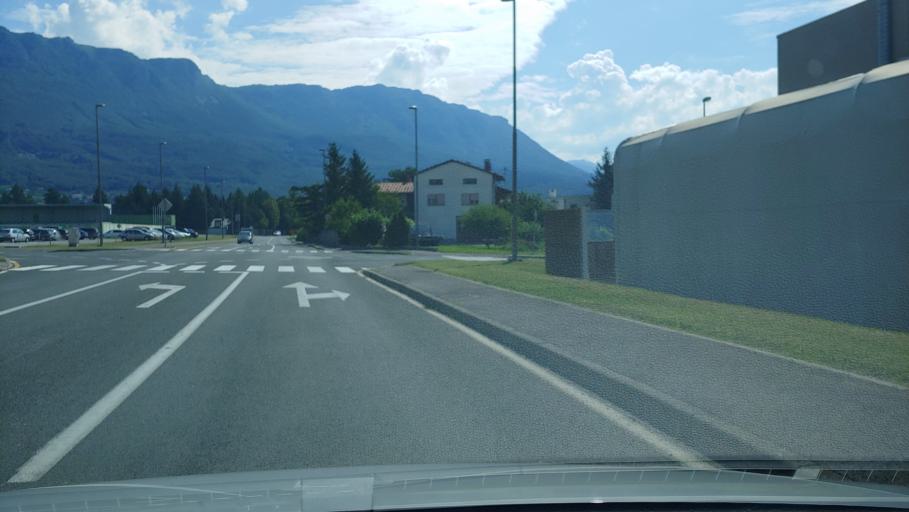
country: SI
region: Ajdovscina
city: Ajdovscina
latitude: 45.8868
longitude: 13.8924
